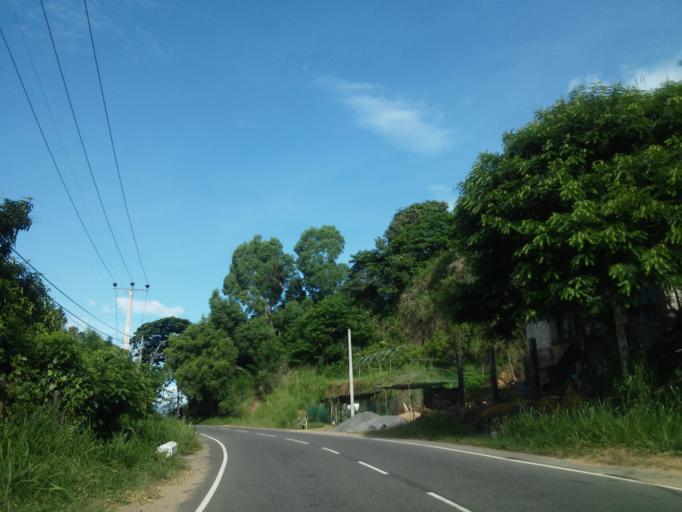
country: LK
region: Uva
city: Haputale
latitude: 6.7630
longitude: 80.9017
